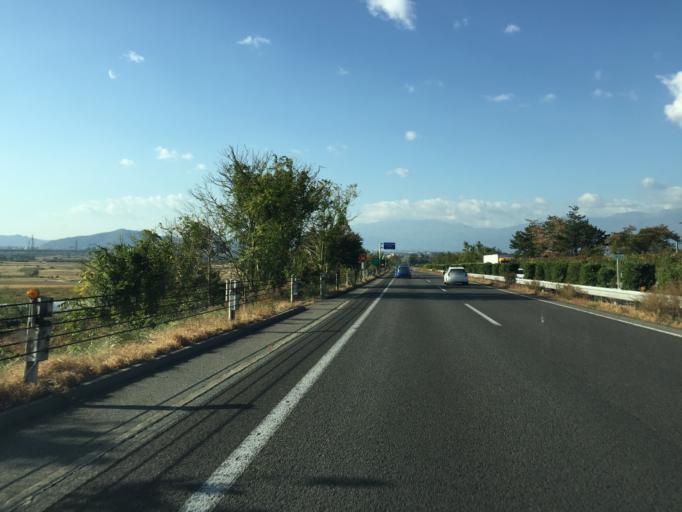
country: JP
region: Fukushima
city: Hobaramachi
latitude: 37.8343
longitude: 140.4912
